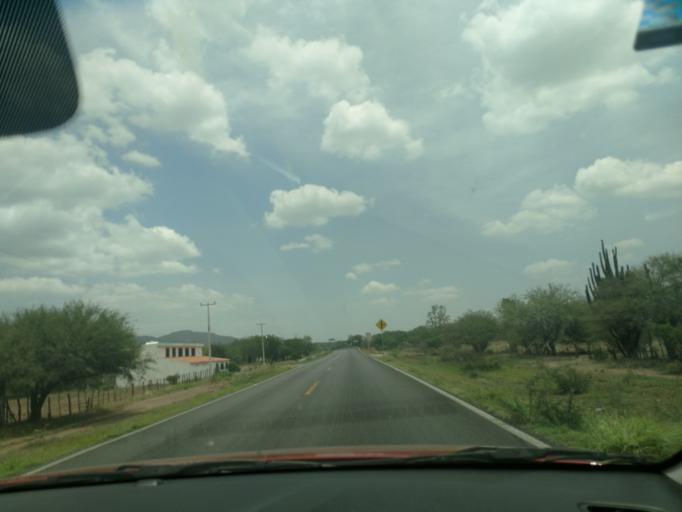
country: MX
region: San Luis Potosi
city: Villa Juarez
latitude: 22.0185
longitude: -100.3895
